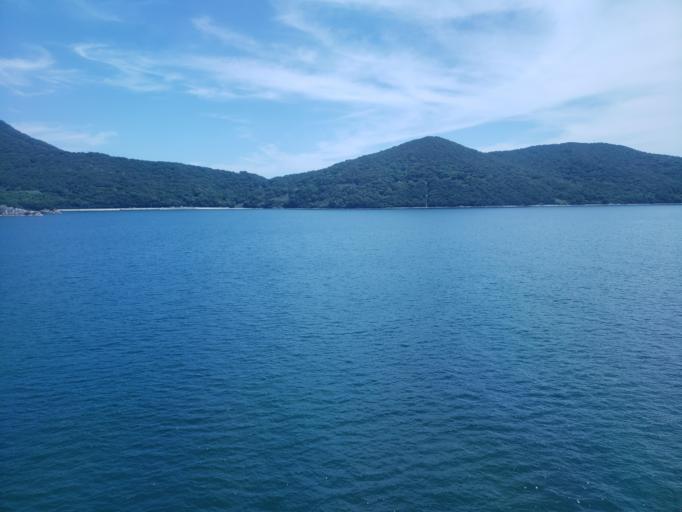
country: JP
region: Kagawa
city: Tonosho
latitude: 34.4410
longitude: 134.3176
